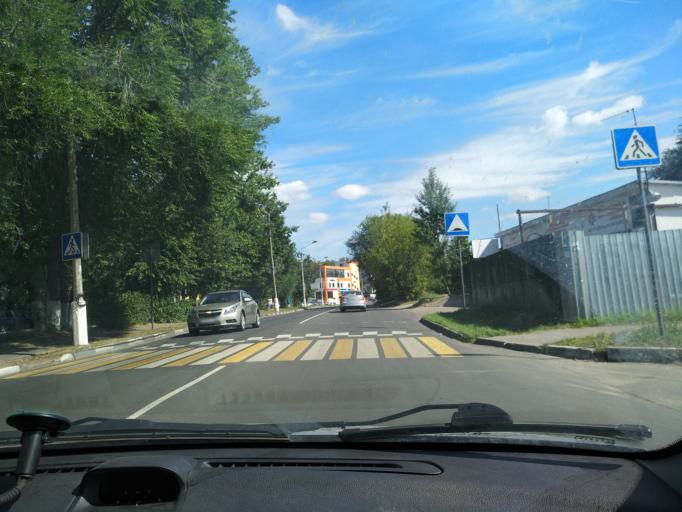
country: RU
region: Moskovskaya
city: Zhukovskiy
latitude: 55.5982
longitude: 38.0972
